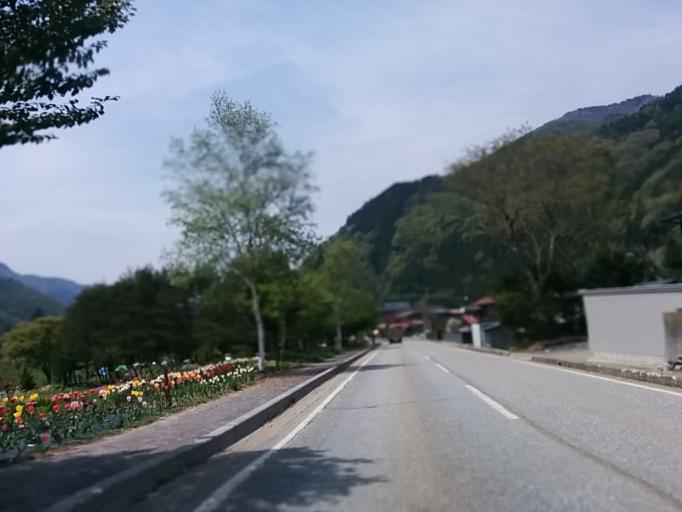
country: JP
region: Gifu
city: Takayama
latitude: 36.2466
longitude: 137.5208
